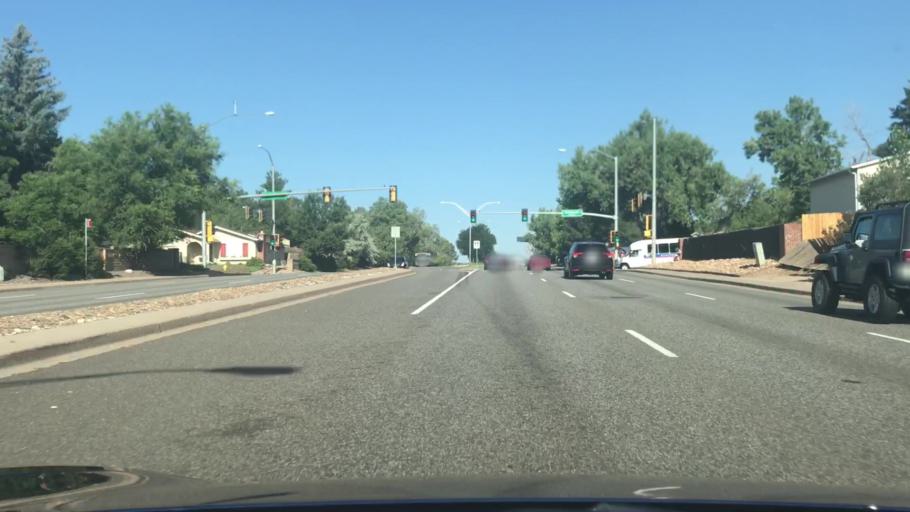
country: US
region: Colorado
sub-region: Arapahoe County
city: Dove Valley
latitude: 39.6531
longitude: -104.8023
